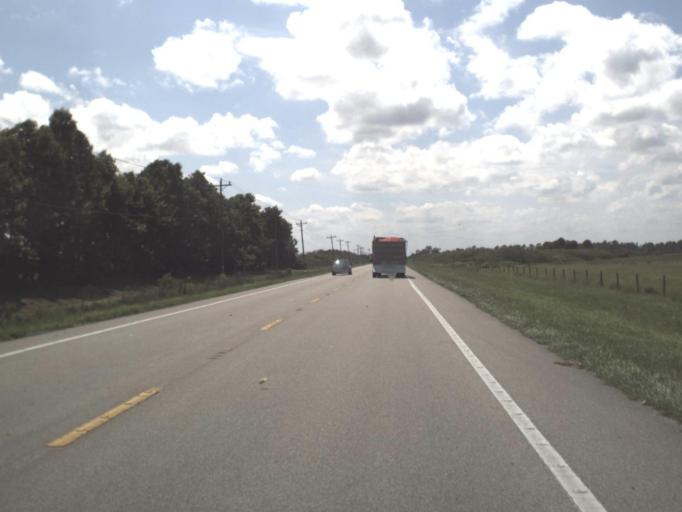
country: US
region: Florida
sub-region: Collier County
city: Immokalee
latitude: 26.5216
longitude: -81.4352
